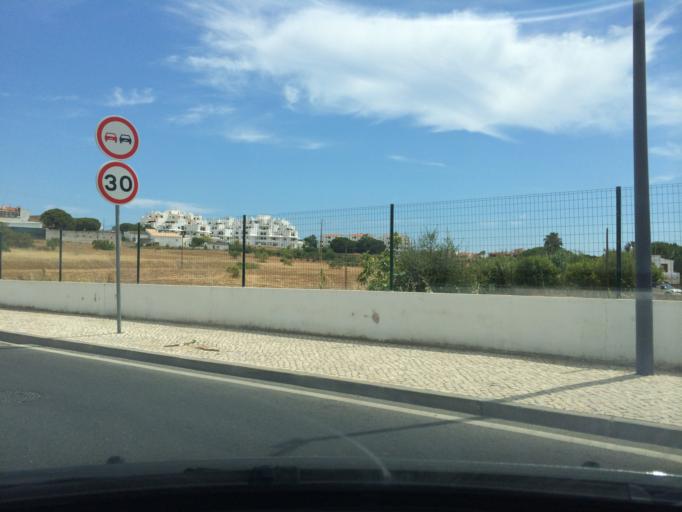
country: PT
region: Faro
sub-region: Albufeira
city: Albufeira
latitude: 37.0938
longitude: -8.1966
